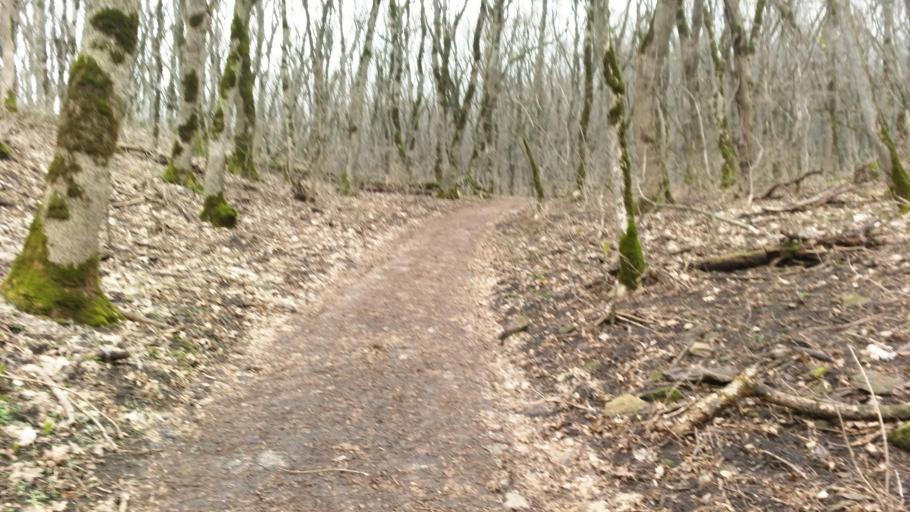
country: RU
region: Stavropol'skiy
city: Zheleznovodsk
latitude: 44.1550
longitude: 43.0441
